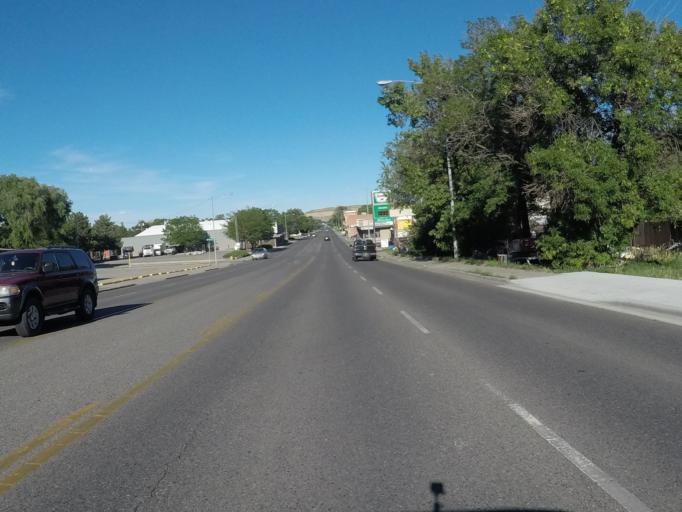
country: US
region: Montana
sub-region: Yellowstone County
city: Billings
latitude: 45.7770
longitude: -108.5420
